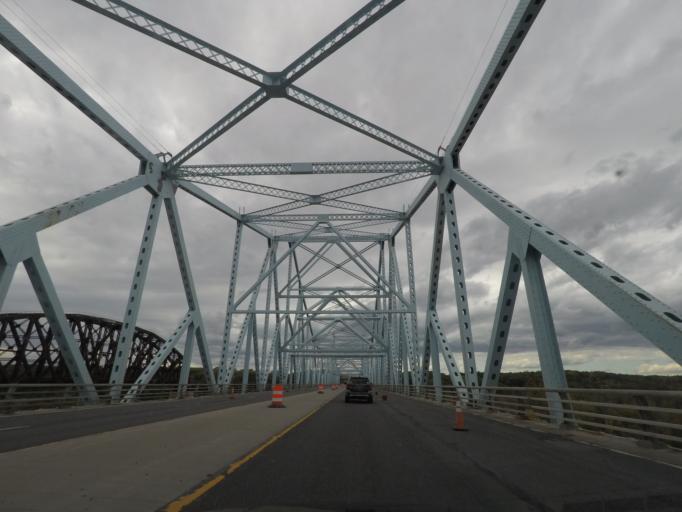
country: US
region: New York
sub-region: Rensselaer County
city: Castleton-on-Hudson
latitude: 42.5092
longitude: -73.7727
